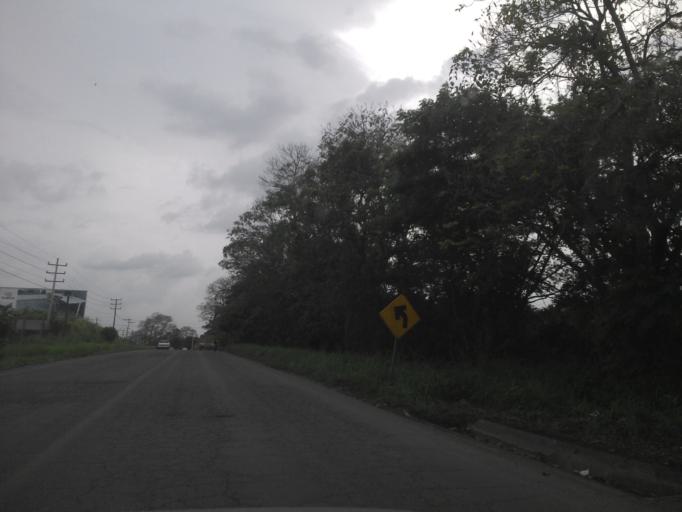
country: MX
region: Veracruz
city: Martinez de la Torre
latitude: 20.0802
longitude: -97.0413
